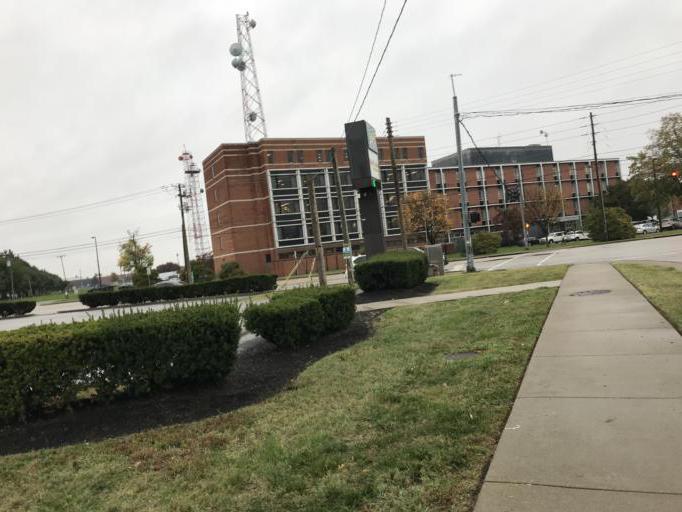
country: US
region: Kentucky
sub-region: Jefferson County
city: West Buechel
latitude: 38.2003
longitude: -85.6844
